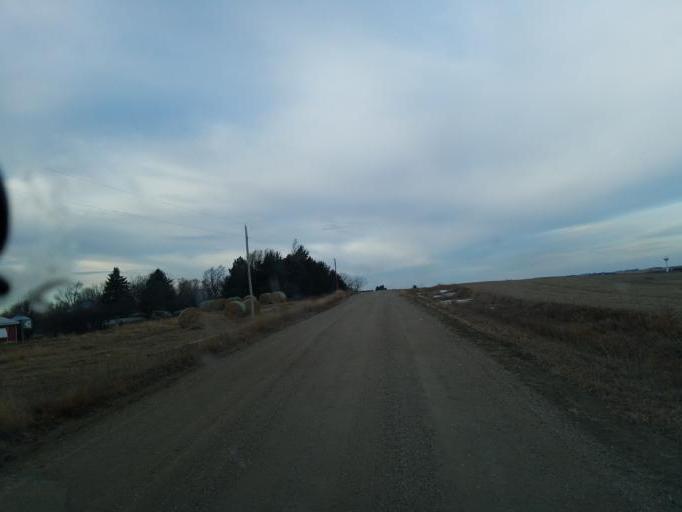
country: US
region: Nebraska
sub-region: Knox County
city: Bloomfield
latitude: 42.5833
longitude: -97.6285
